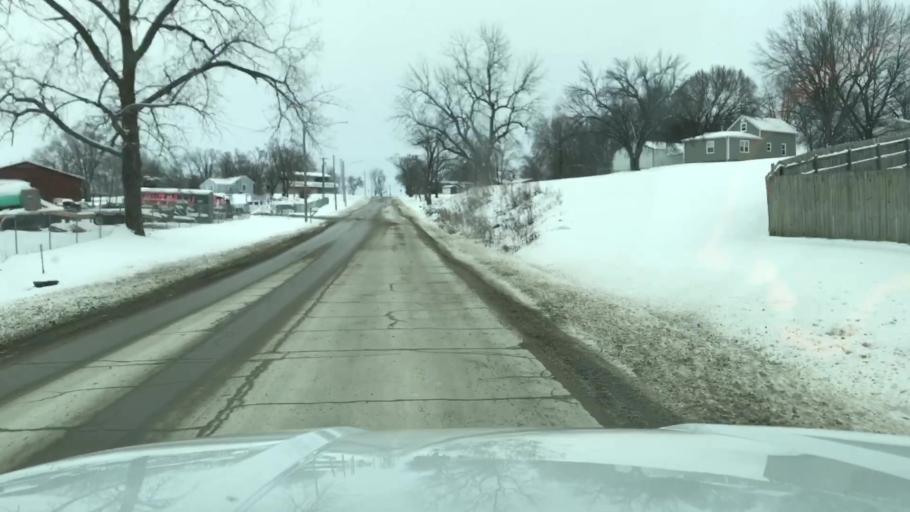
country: US
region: Missouri
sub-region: Clinton County
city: Cameron
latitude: 39.7474
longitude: -94.2324
